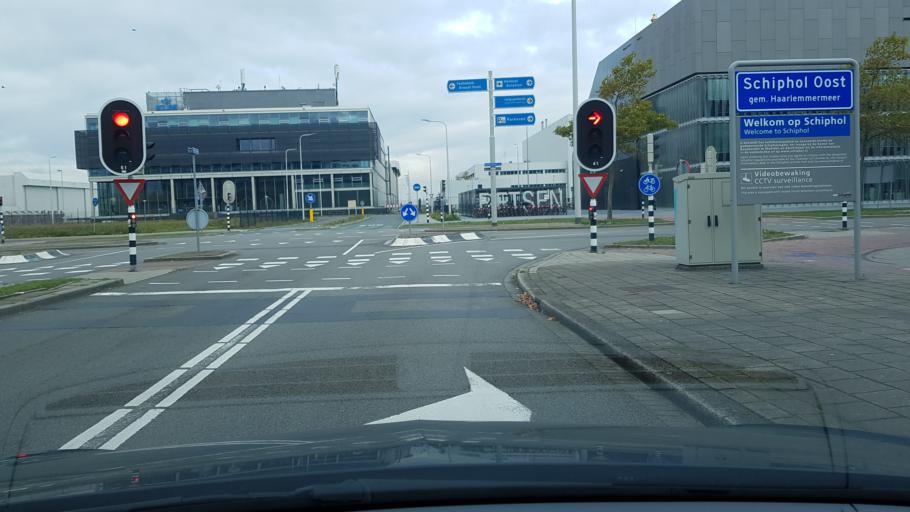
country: NL
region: North Holland
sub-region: Gemeente Amstelveen
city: Amstelveen
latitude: 52.3069
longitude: 4.8081
